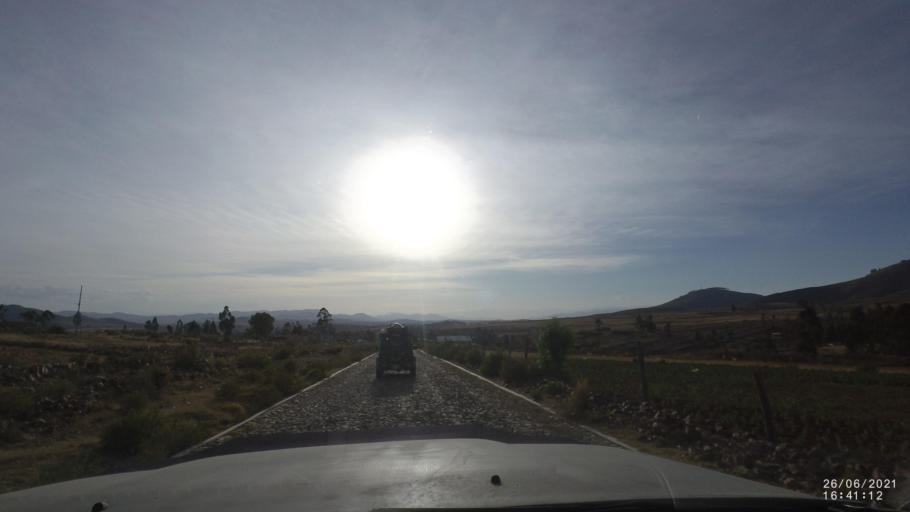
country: BO
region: Cochabamba
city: Arani
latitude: -17.7679
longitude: -65.8188
